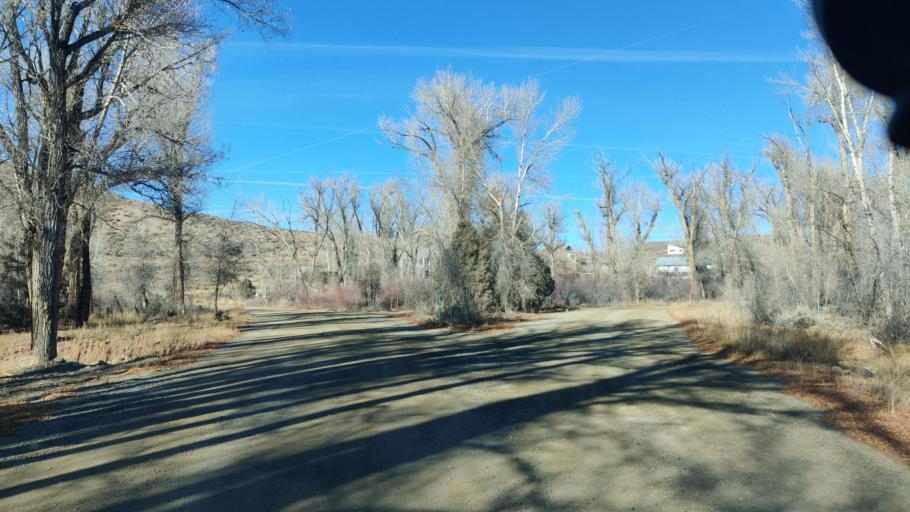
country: US
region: Colorado
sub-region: Gunnison County
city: Gunnison
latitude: 38.5403
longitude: -106.9508
